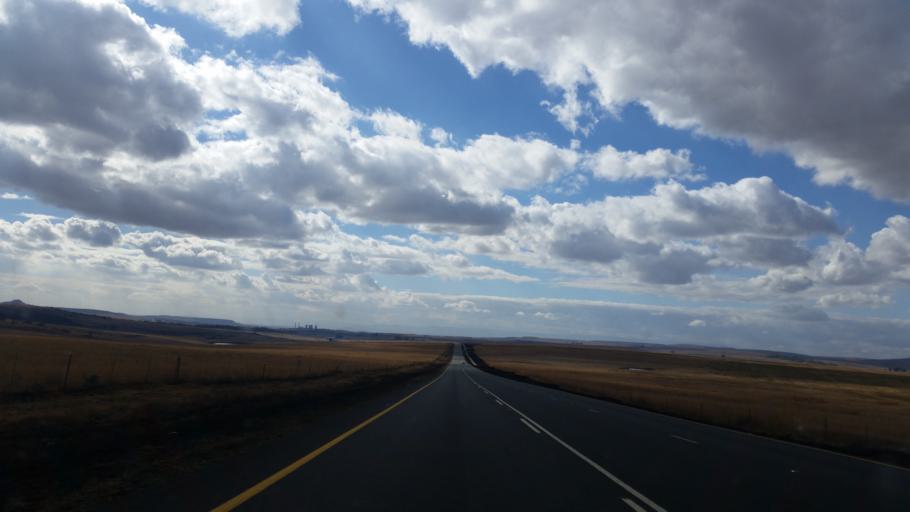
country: ZA
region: KwaZulu-Natal
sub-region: Amajuba District Municipality
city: Dannhauser
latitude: -27.9577
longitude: 29.9695
